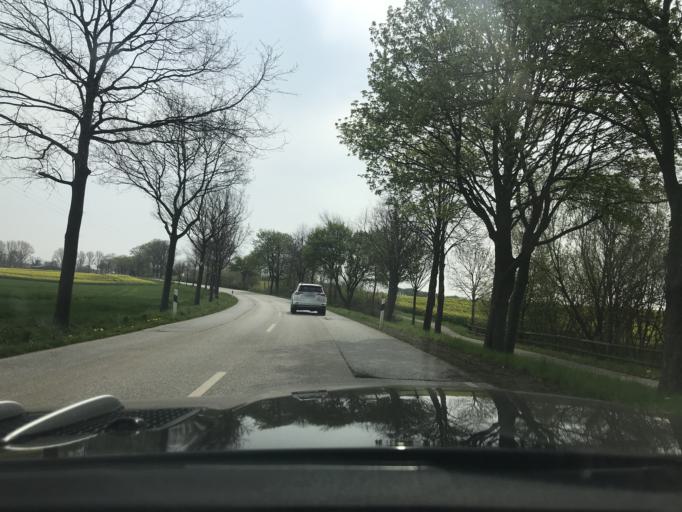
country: DE
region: Schleswig-Holstein
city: Heringsdorf
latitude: 54.2817
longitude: 11.0209
